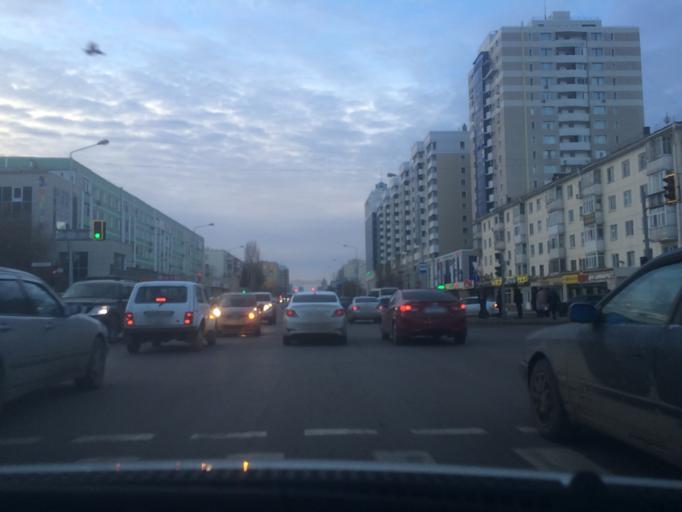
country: KZ
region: Astana Qalasy
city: Astana
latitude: 51.1695
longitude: 71.4079
